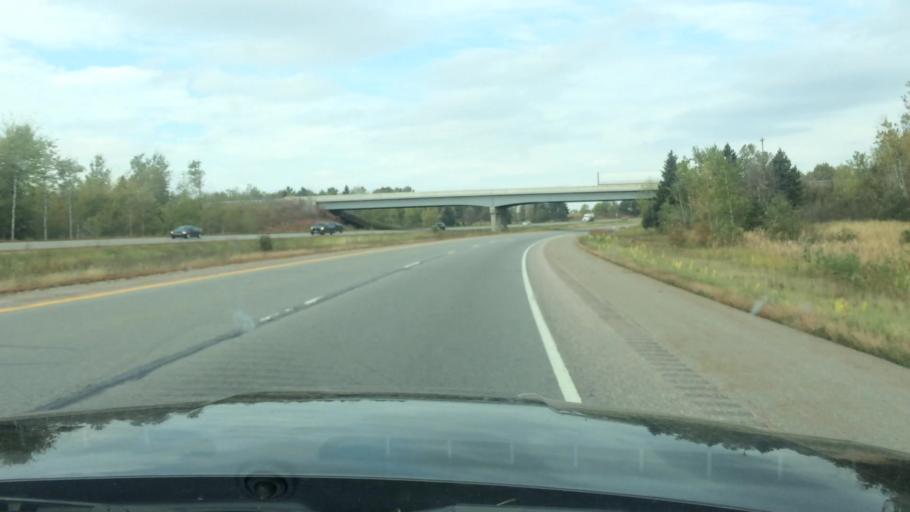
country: US
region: Wisconsin
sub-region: Marathon County
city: Mosinee
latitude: 44.7277
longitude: -89.6772
